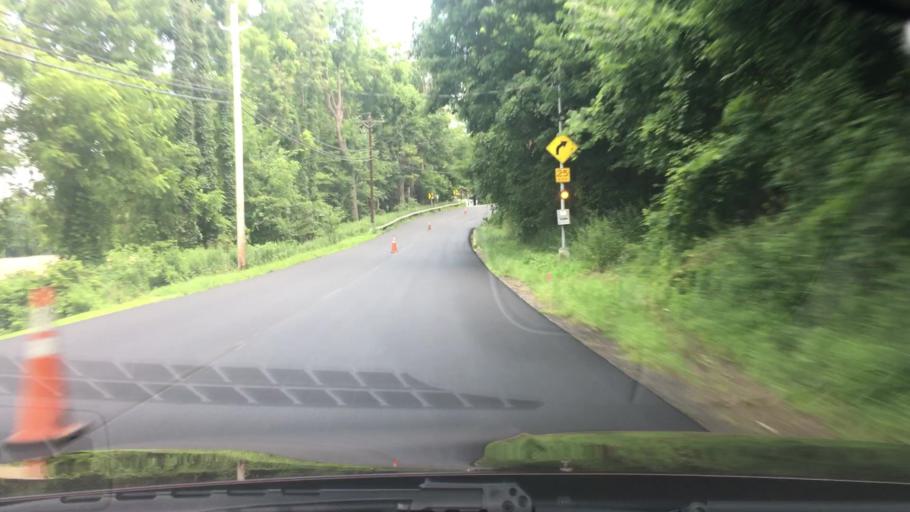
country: US
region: New York
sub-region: Dutchess County
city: Hillside Lake
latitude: 41.5779
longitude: -73.7459
